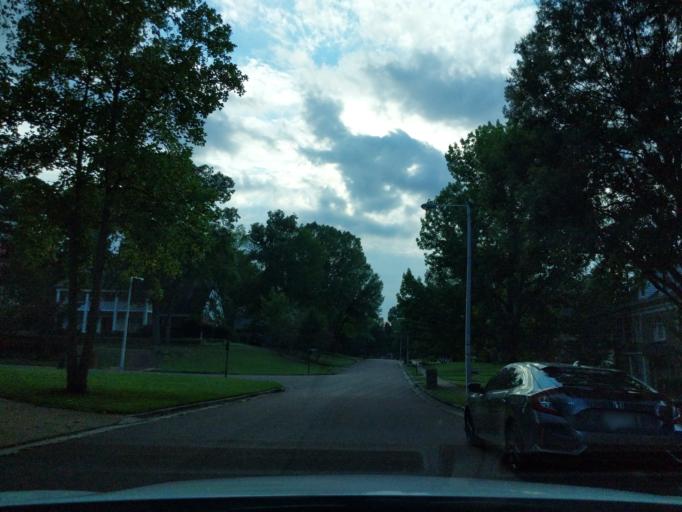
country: US
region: Tennessee
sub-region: Shelby County
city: Germantown
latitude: 35.0669
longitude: -89.7789
